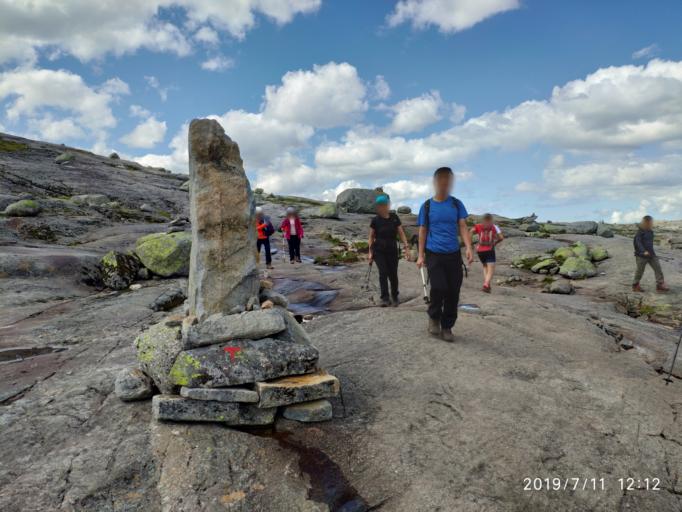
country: NO
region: Vest-Agder
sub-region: Sirdal
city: Tonstad
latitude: 59.0343
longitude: 6.6005
